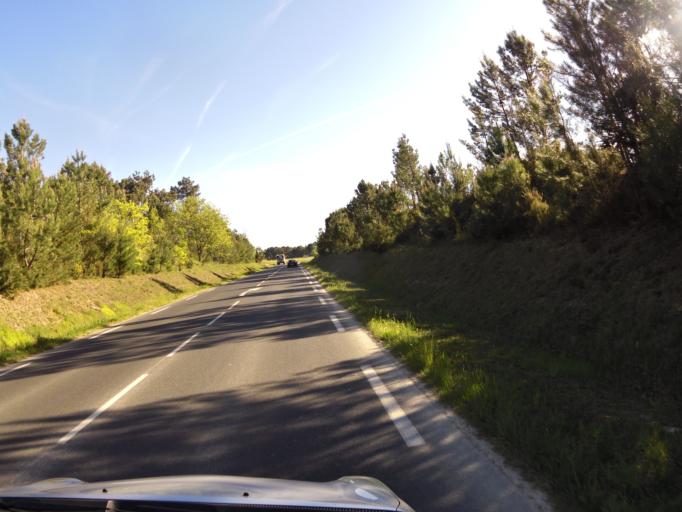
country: FR
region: Aquitaine
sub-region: Departement de la Dordogne
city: Sarlat-la-Caneda
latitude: 44.9548
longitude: 1.2263
